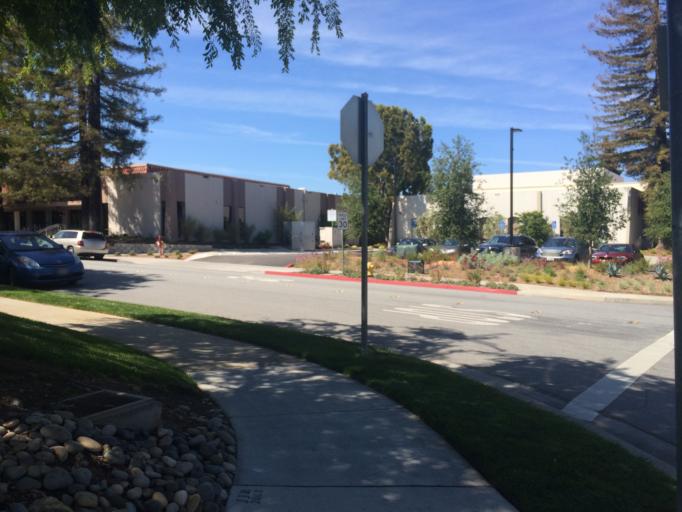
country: US
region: California
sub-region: Santa Clara County
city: Cupertino
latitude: 37.3323
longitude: -122.0346
